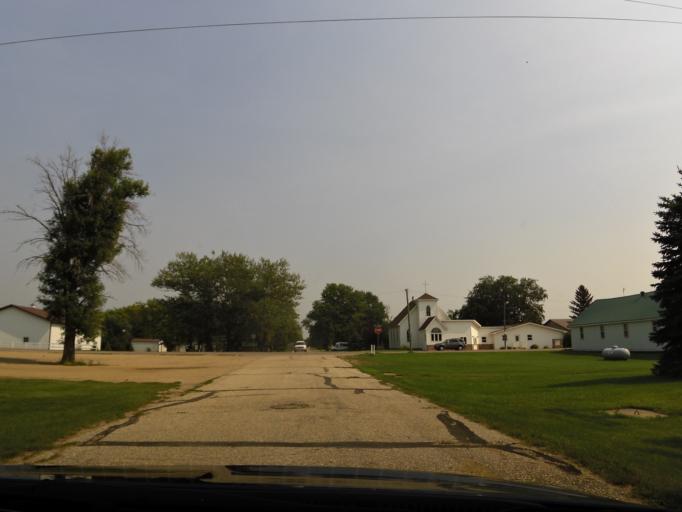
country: US
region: South Dakota
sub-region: Roberts County
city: Sisseton
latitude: 45.8579
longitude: -97.1046
